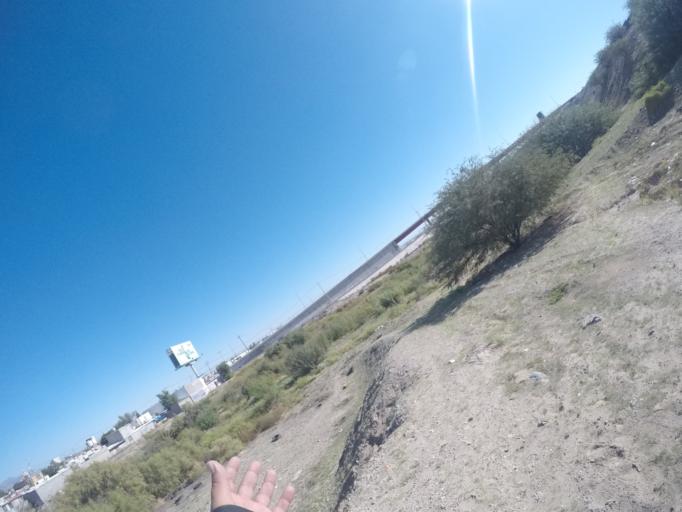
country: US
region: Texas
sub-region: El Paso County
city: Socorro
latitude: 31.6703
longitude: -106.4034
